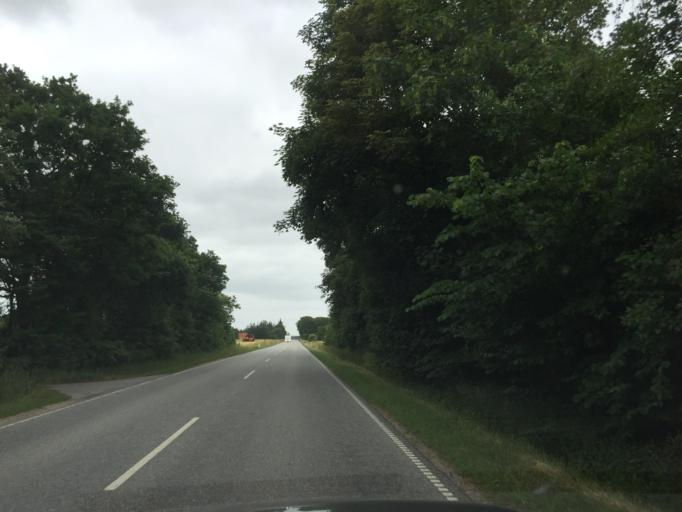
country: DK
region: South Denmark
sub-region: Esbjerg Kommune
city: Ribe
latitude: 55.3624
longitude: 8.7985
